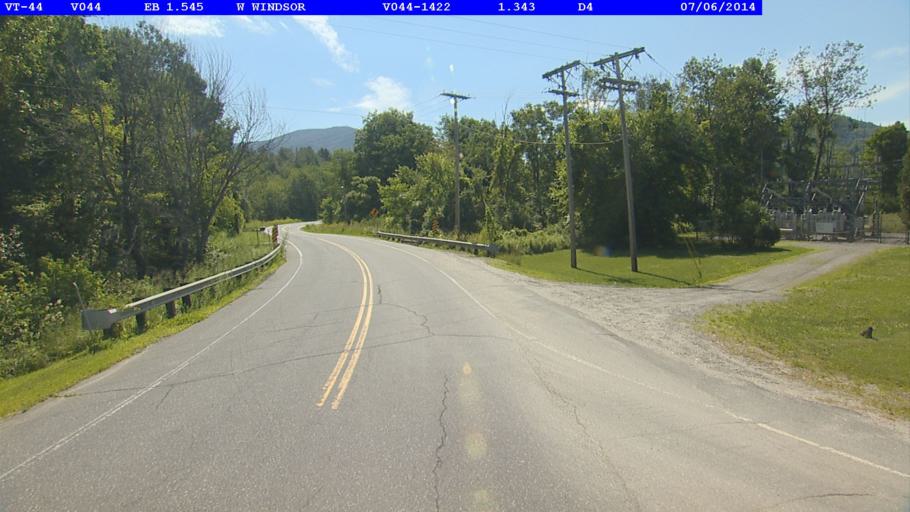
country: US
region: Vermont
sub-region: Windsor County
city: Windsor
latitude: 43.4556
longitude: -72.5155
